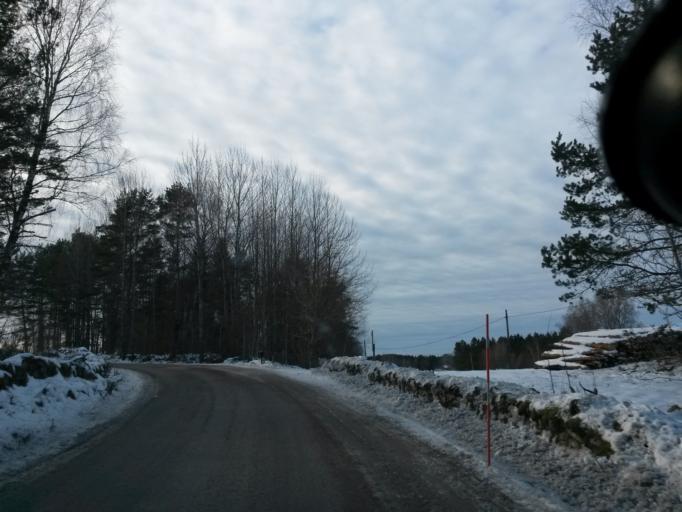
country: SE
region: Vaestra Goetaland
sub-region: Vargarda Kommun
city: Vargarda
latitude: 58.0091
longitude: 12.8882
